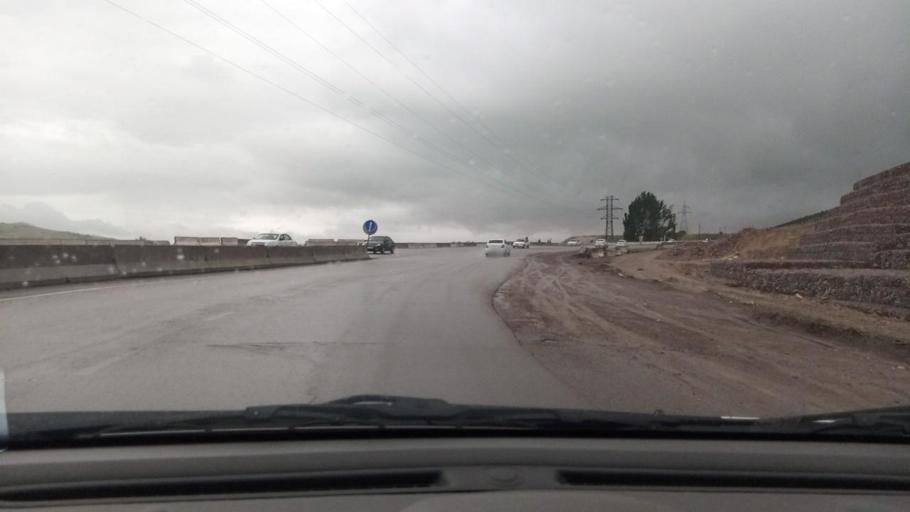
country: UZ
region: Toshkent
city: Angren
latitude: 41.0698
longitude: 70.2422
